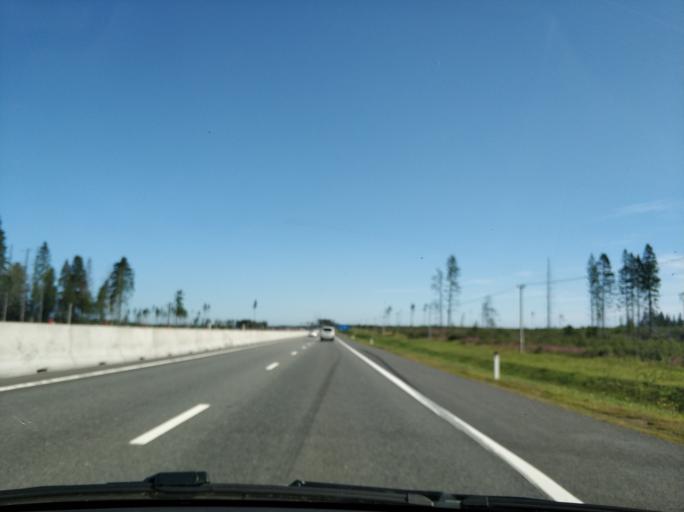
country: RU
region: Leningrad
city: Sosnovo
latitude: 60.4938
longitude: 30.1959
